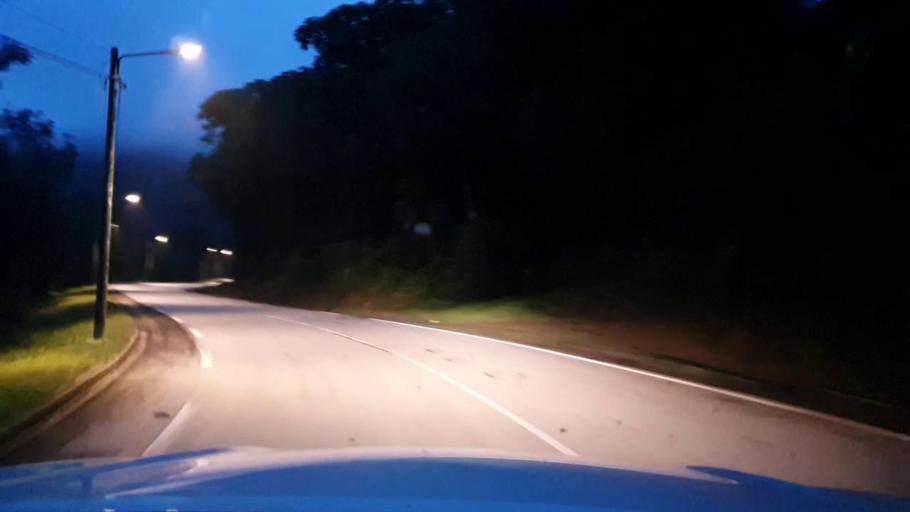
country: RW
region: Southern Province
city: Nzega
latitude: -2.5318
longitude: 29.3924
